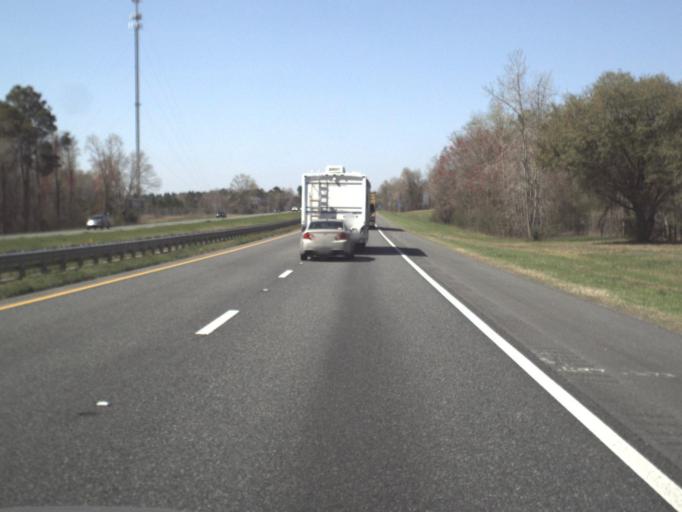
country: US
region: Florida
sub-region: Washington County
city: Chipley
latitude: 30.7524
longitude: -85.3862
